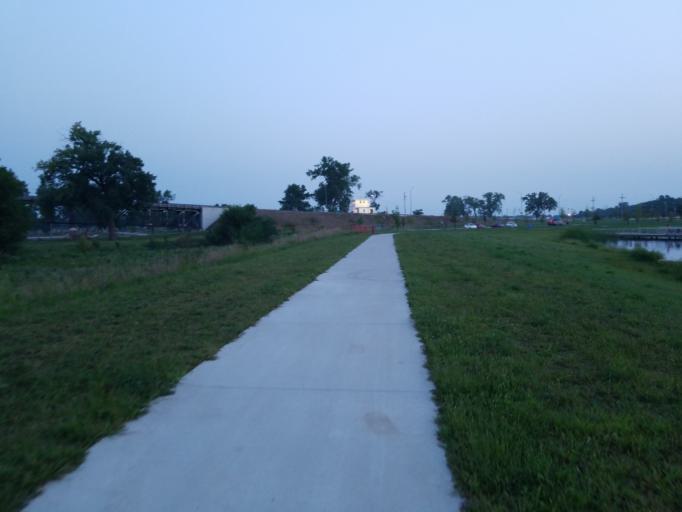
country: US
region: Nebraska
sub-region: Sarpy County
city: Bellevue
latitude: 41.1389
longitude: -95.8827
